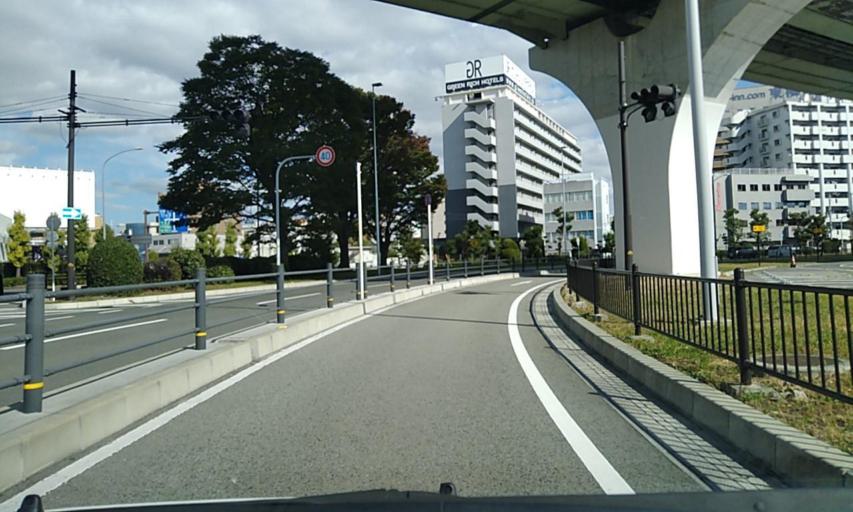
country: JP
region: Osaka
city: Ikeda
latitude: 34.7940
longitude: 135.4404
